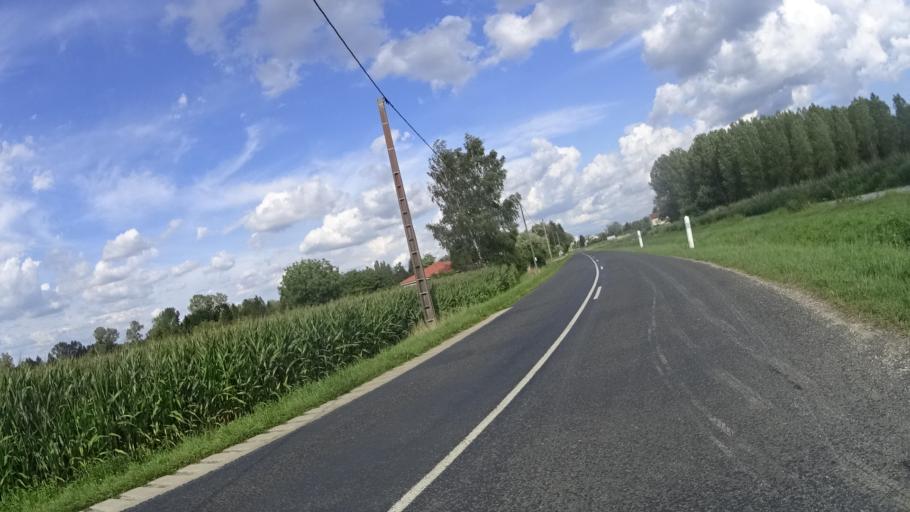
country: FR
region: Champagne-Ardenne
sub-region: Departement de la Marne
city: Sermaize-les-Bains
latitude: 48.7892
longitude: 4.8952
